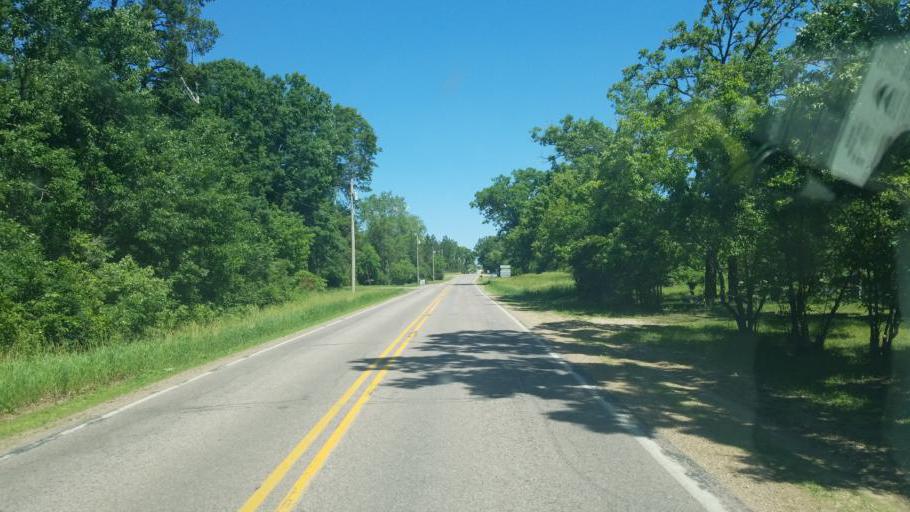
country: US
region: Wisconsin
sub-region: Adams County
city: Friendship
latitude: 43.9789
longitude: -89.9381
